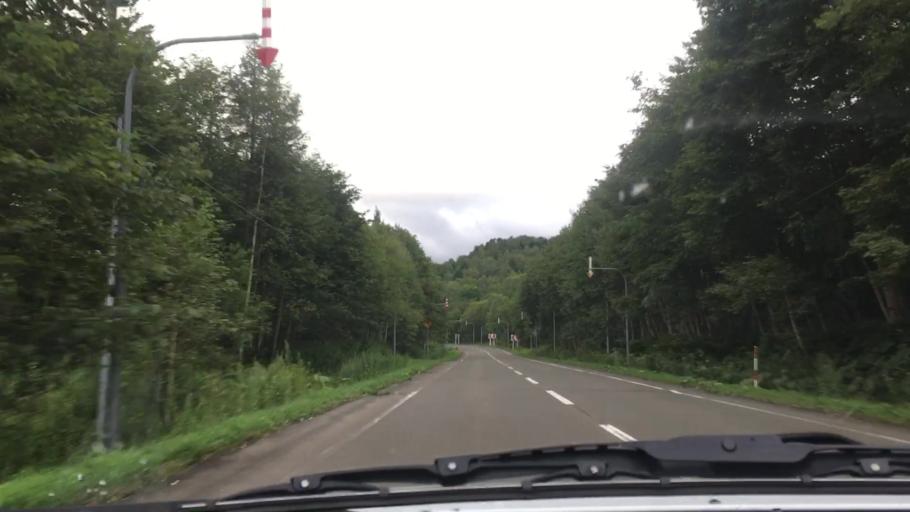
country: JP
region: Hokkaido
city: Shimo-furano
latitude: 43.0621
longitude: 142.6688
